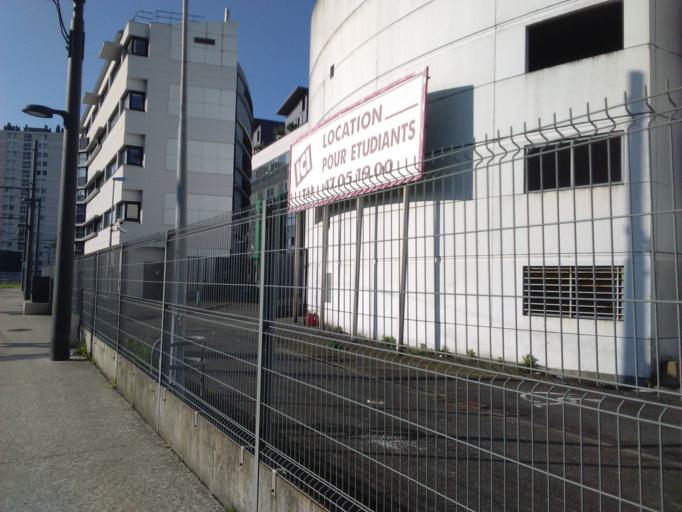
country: FR
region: Centre
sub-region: Departement d'Indre-et-Loire
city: Tours
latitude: 47.3877
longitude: 0.6943
